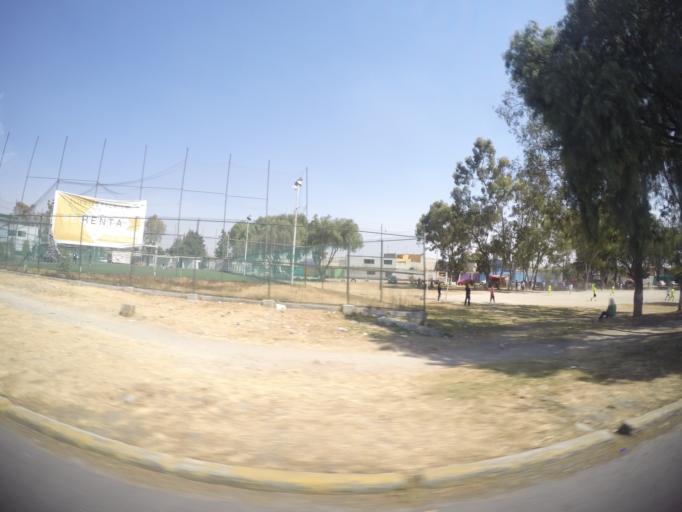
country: MX
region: Mexico
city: Ecatepec
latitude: 19.6004
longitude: -99.0334
